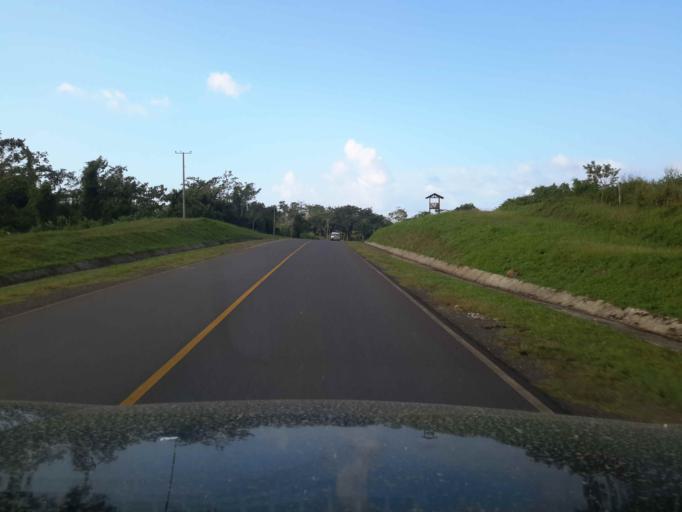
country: NI
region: Rio San Juan
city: San Carlos
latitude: 11.1886
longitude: -84.6782
